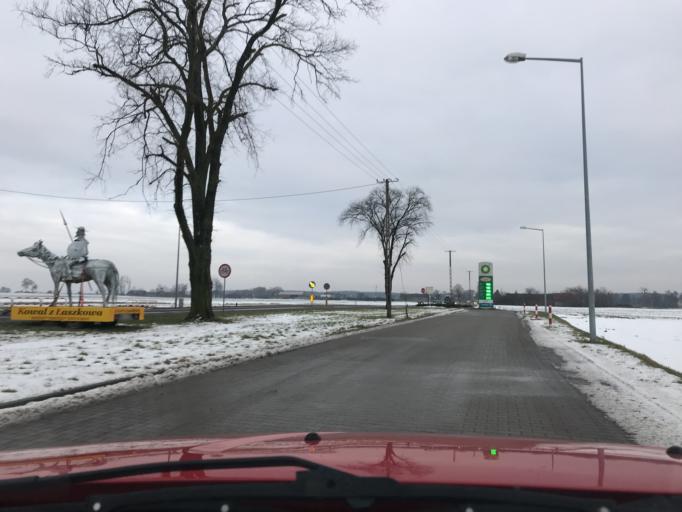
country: PL
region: Greater Poland Voivodeship
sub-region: Powiat pleszewski
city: Pleszew
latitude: 51.8890
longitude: 17.8441
